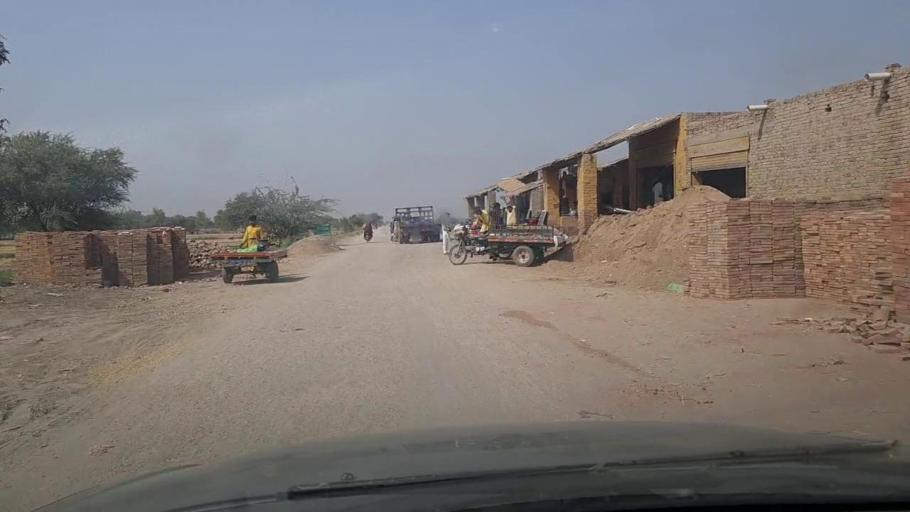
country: PK
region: Sindh
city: Mirpur Mathelo
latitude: 27.9136
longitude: 69.5178
